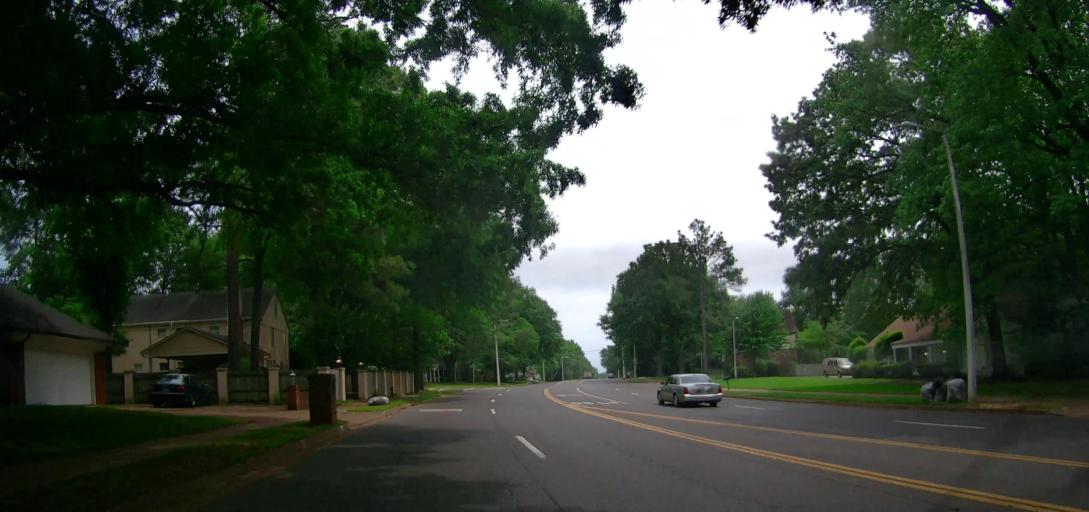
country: US
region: Tennessee
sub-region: Shelby County
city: Germantown
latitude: 35.0844
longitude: -89.8528
